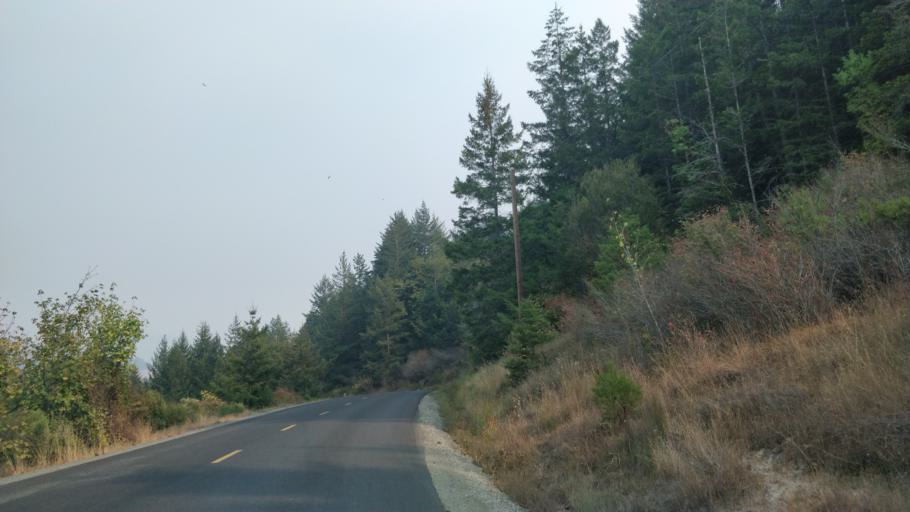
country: US
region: California
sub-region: Humboldt County
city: Rio Dell
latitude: 40.2522
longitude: -124.1870
